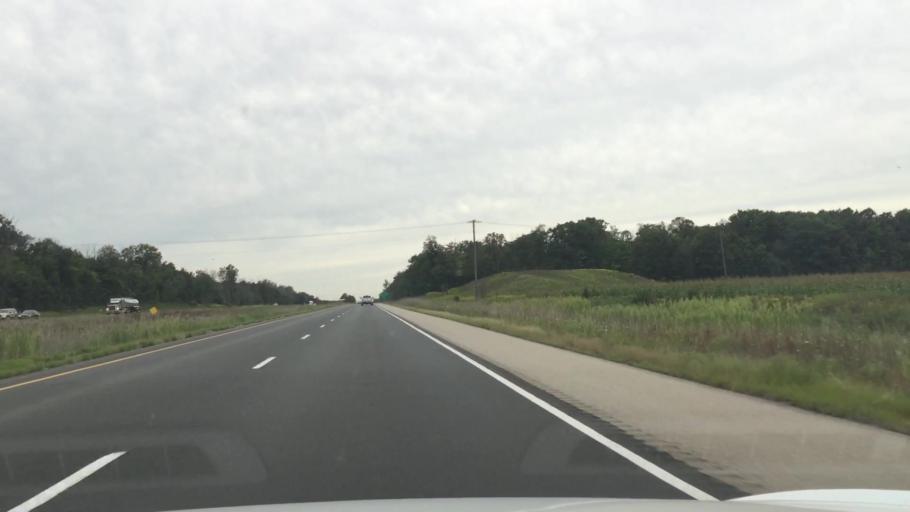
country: CA
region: Ontario
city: Lambton Shores
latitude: 42.9923
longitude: -81.8552
